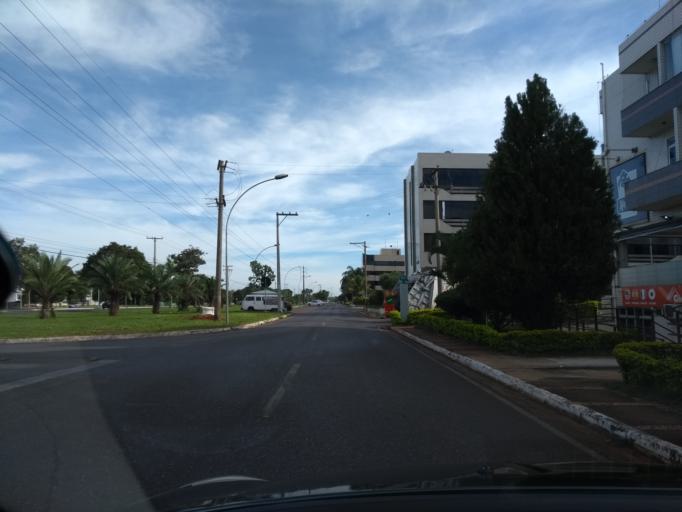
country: BR
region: Federal District
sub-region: Brasilia
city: Brasilia
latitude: -15.7905
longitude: -47.9323
